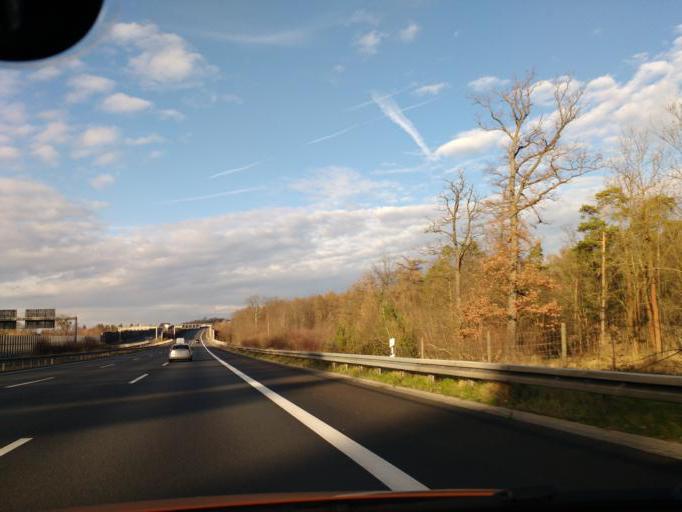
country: DE
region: Lower Saxony
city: Helmstedt
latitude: 52.2293
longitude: 11.0334
